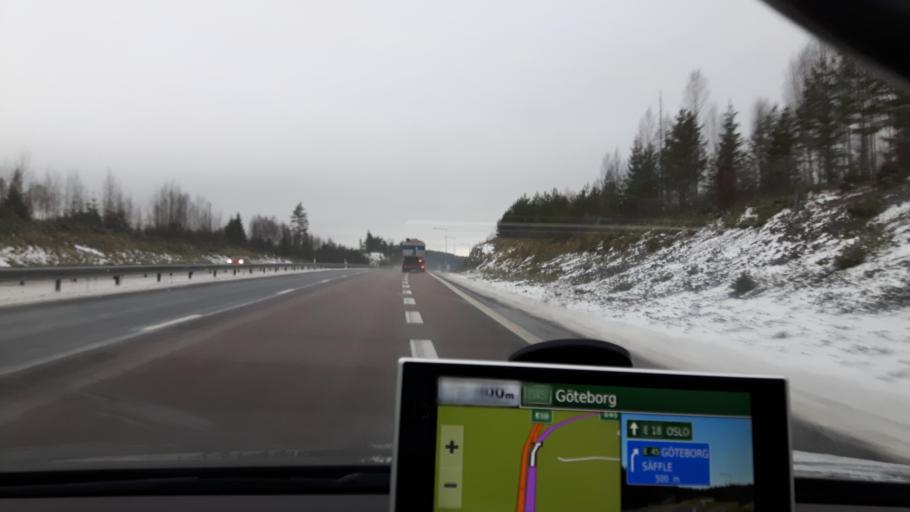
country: SE
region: Vaermland
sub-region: Grums Kommun
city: Slottsbron
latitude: 59.2663
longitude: 13.0082
